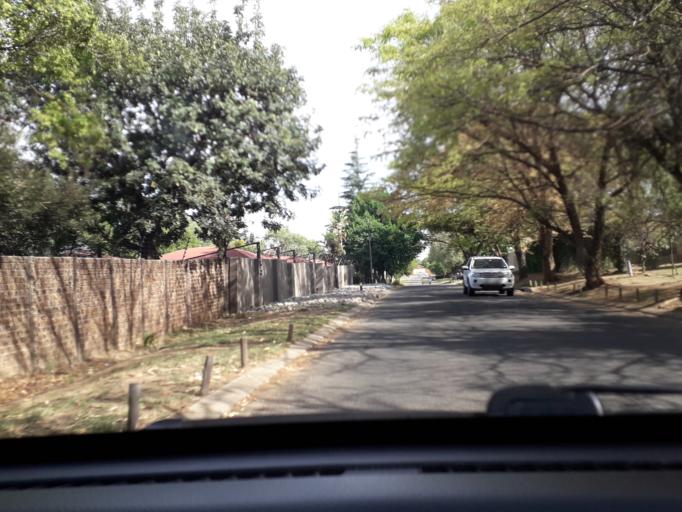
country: ZA
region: Gauteng
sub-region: City of Johannesburg Metropolitan Municipality
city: Diepsloot
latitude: -26.0435
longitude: 28.0102
